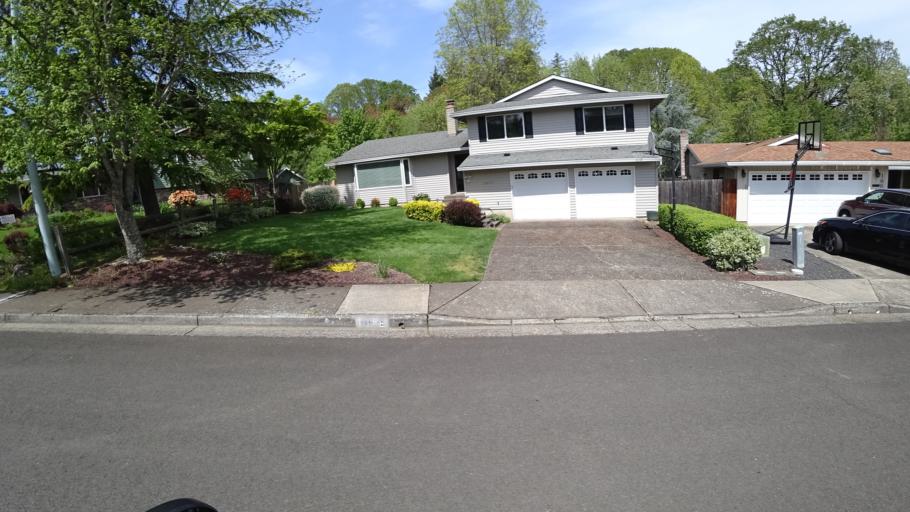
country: US
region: Oregon
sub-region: Washington County
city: Aloha
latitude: 45.4610
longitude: -122.8480
